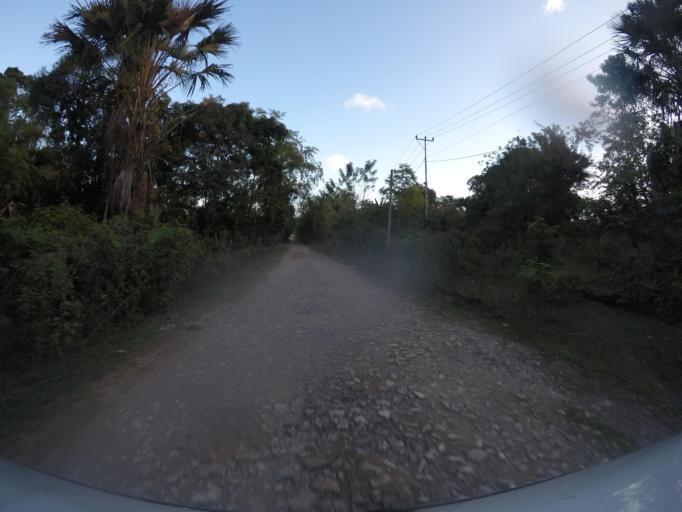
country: TL
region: Baucau
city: Venilale
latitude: -8.7250
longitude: 126.7087
